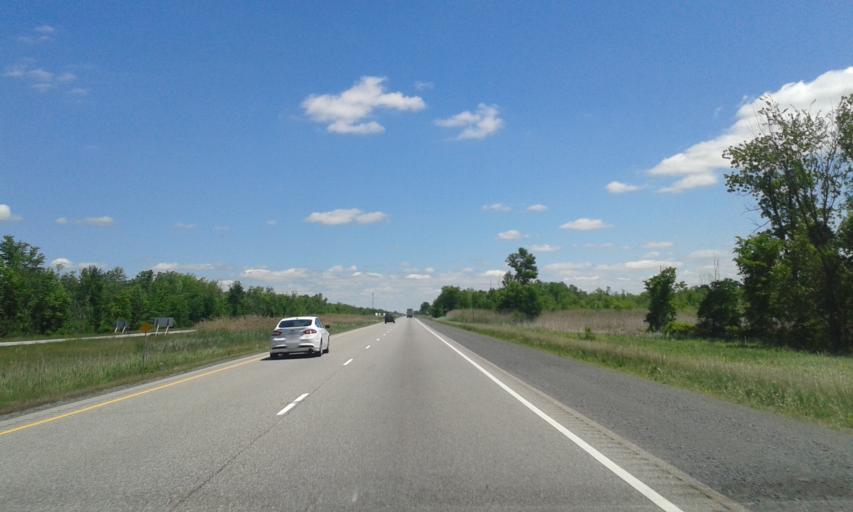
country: US
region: New York
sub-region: St. Lawrence County
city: Massena
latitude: 44.9944
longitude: -75.0391
